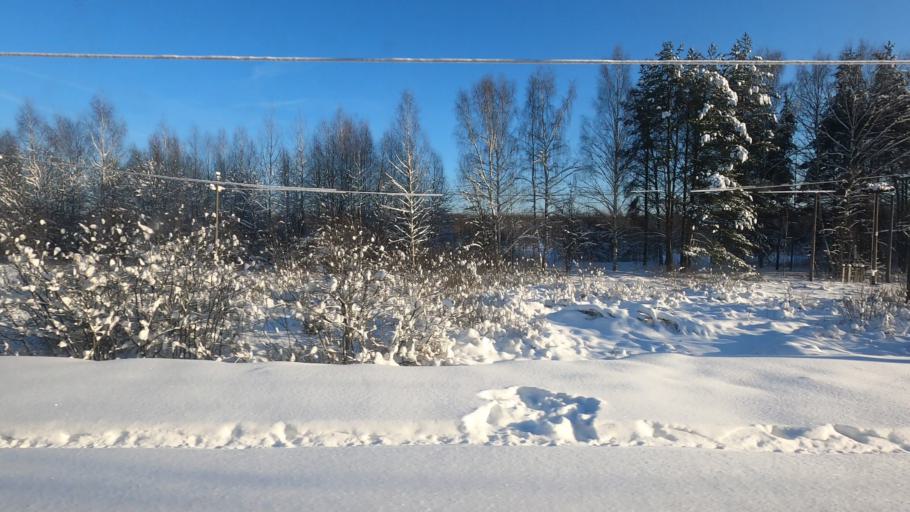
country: RU
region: Moskovskaya
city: Novo-Nikol'skoye
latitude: 56.6411
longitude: 37.5619
